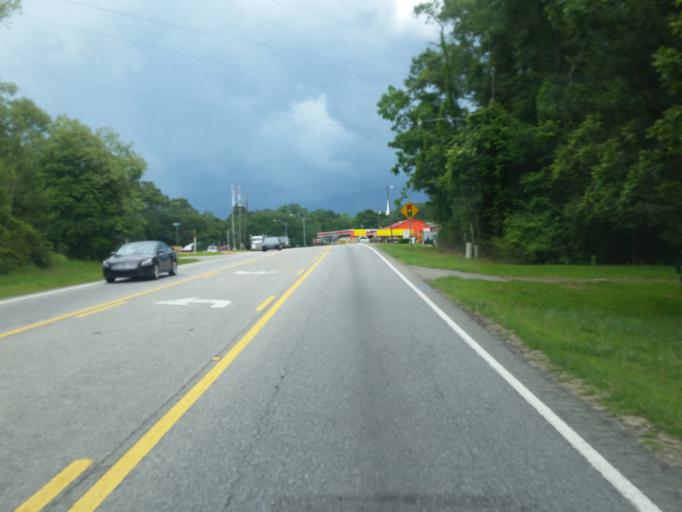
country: US
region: Mississippi
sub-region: Jackson County
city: Hurley
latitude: 30.8240
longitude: -88.3637
